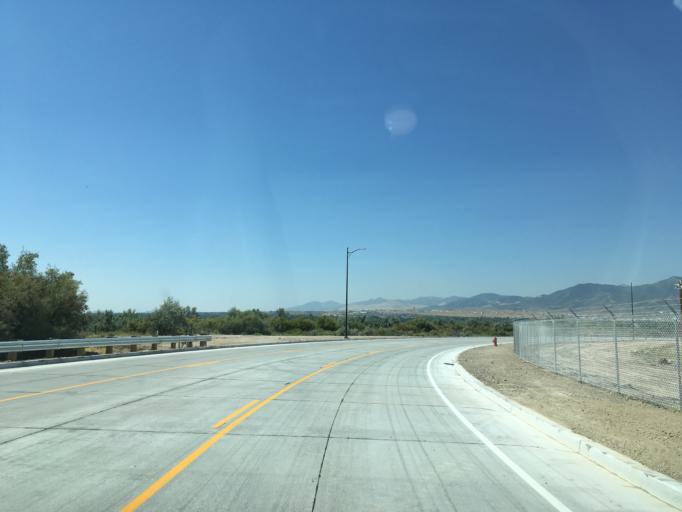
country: US
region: Utah
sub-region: Salt Lake County
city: West Valley City
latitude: 40.7193
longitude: -112.0059
